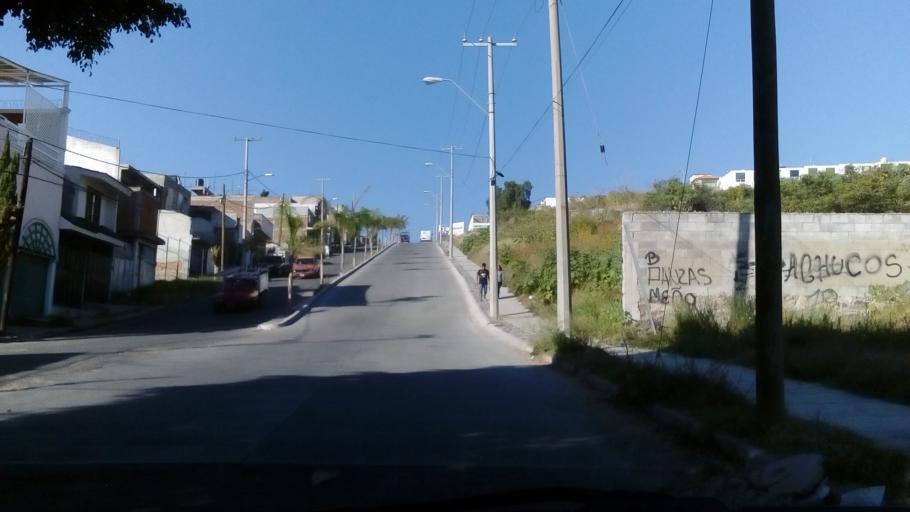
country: MX
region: Guanajuato
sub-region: Leon
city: Ejido la Joya
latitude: 21.1125
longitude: -101.7138
